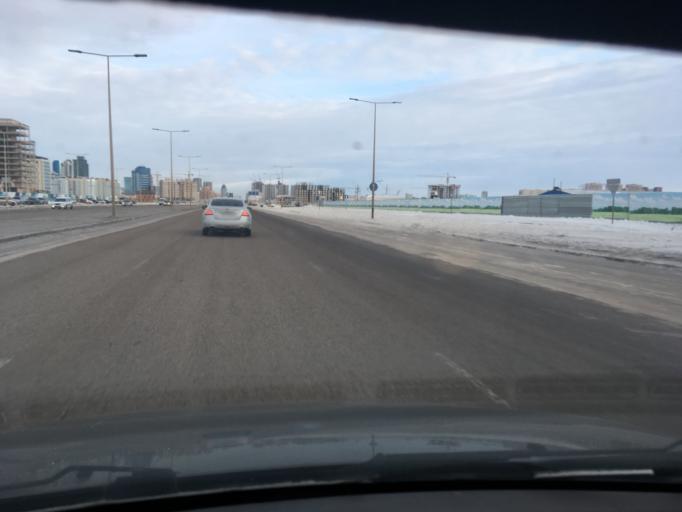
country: KZ
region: Astana Qalasy
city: Astana
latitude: 51.1299
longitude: 71.3817
